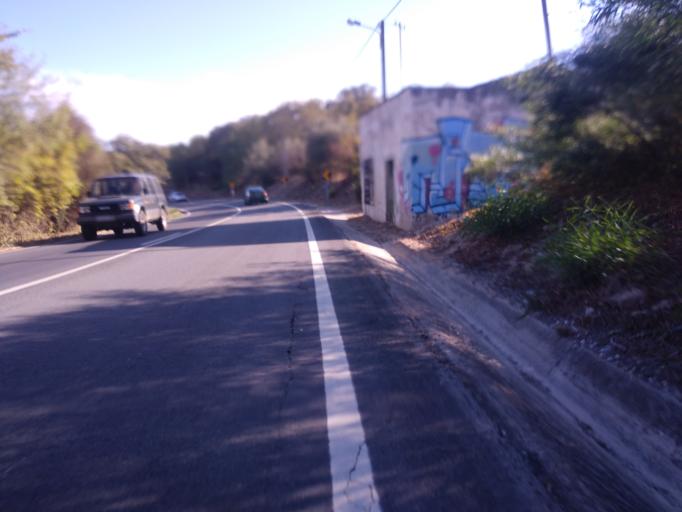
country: PT
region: Faro
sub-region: Sao Bras de Alportel
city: Sao Bras de Alportel
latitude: 37.1087
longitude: -7.9082
